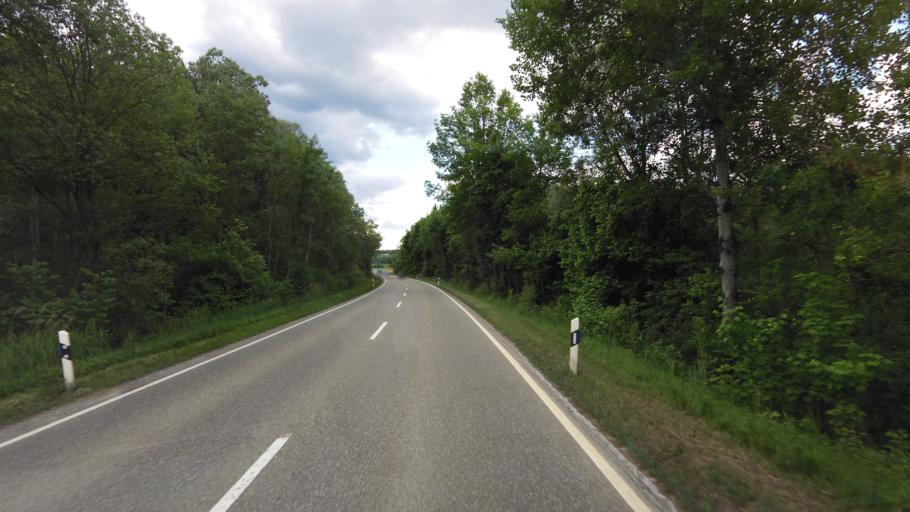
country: DE
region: Bavaria
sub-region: Upper Bavaria
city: Griesstatt
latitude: 47.9969
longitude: 12.1610
